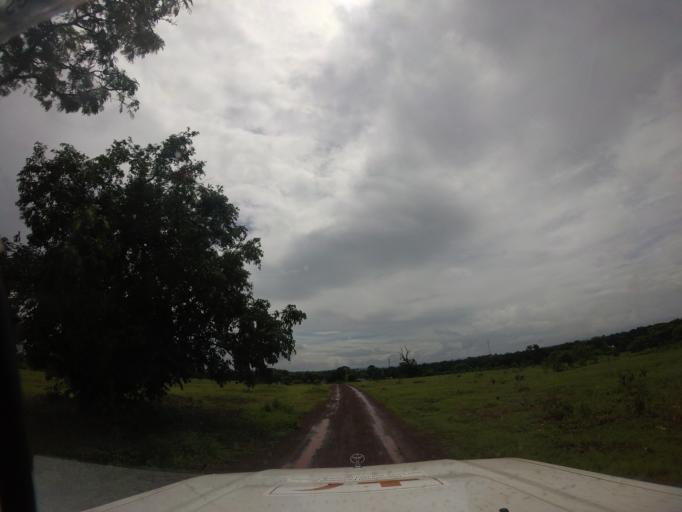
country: SL
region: Northern Province
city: Loma
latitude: 9.8761
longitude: -12.4389
